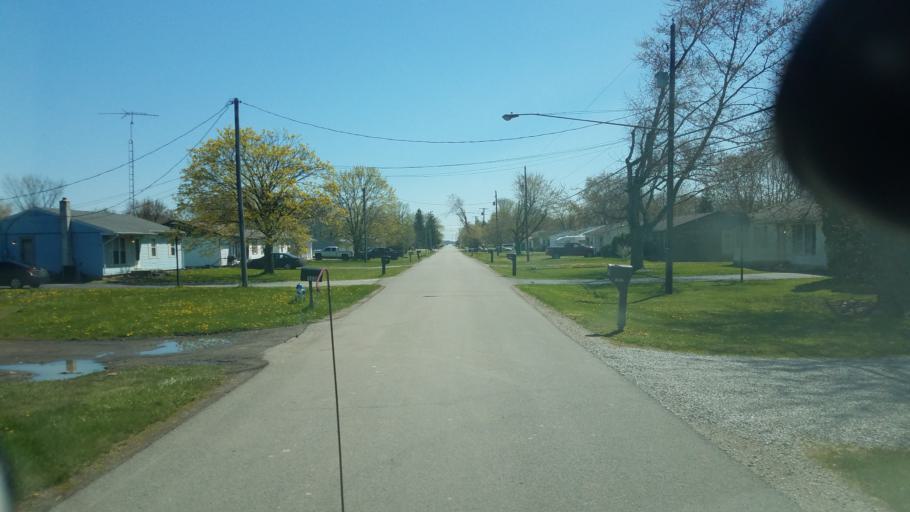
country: US
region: Ohio
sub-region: Marion County
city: Marion
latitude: 40.6392
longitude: -83.0832
